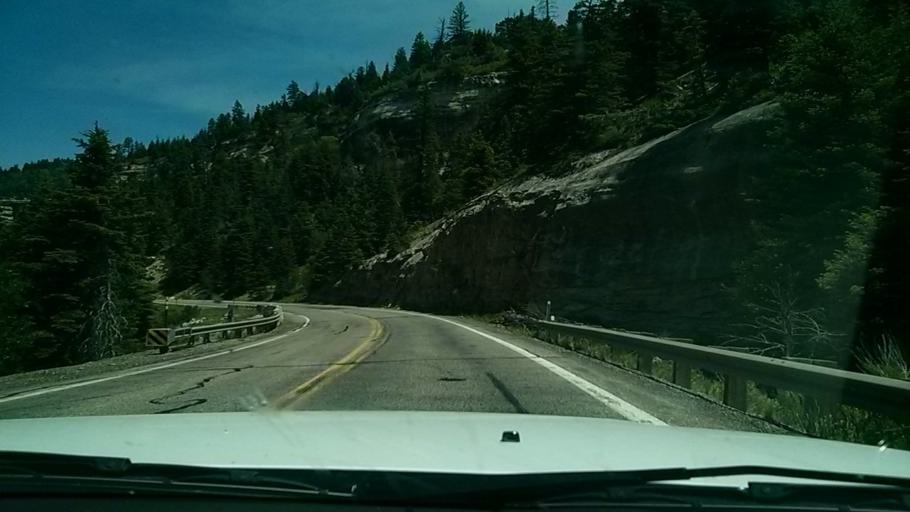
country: US
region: Utah
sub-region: Iron County
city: Cedar City
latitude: 37.6098
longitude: -112.9342
